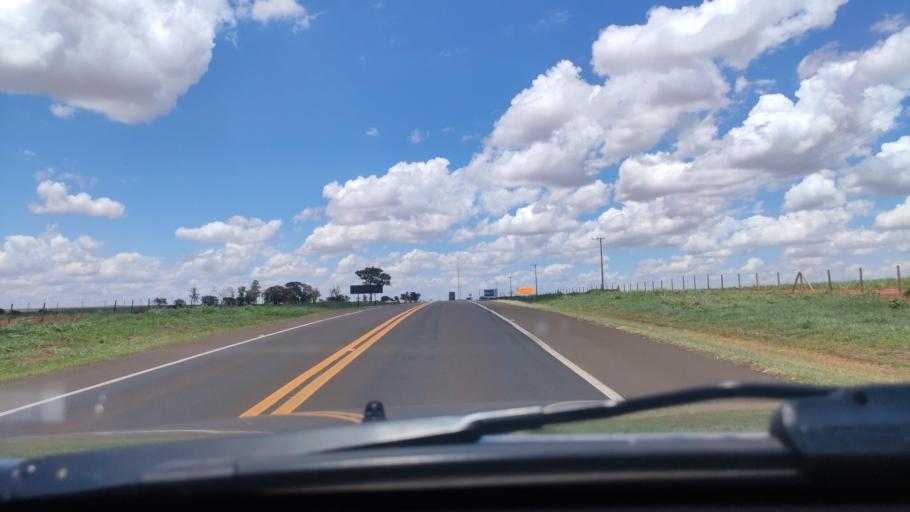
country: BR
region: Sao Paulo
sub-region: Jau
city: Jau
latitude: -22.1821
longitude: -48.4924
